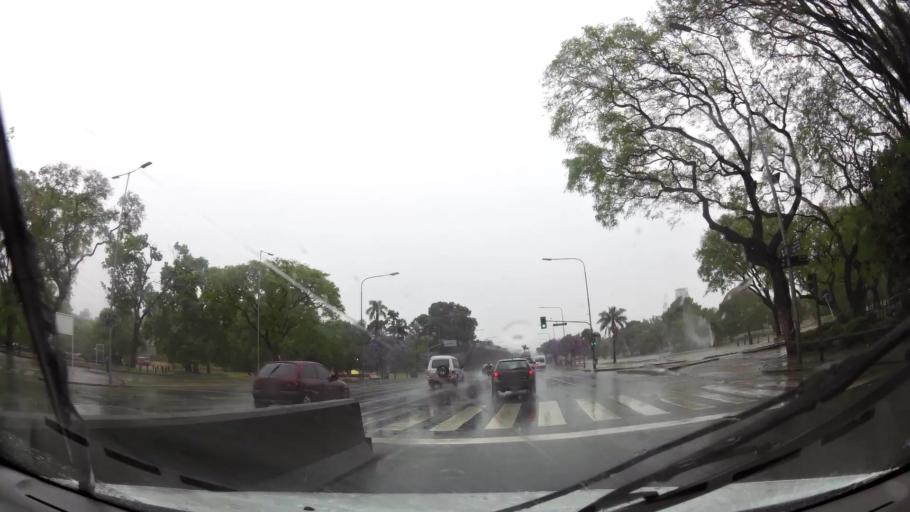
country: AR
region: Buenos Aires F.D.
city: Retiro
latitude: -34.5689
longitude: -58.4094
